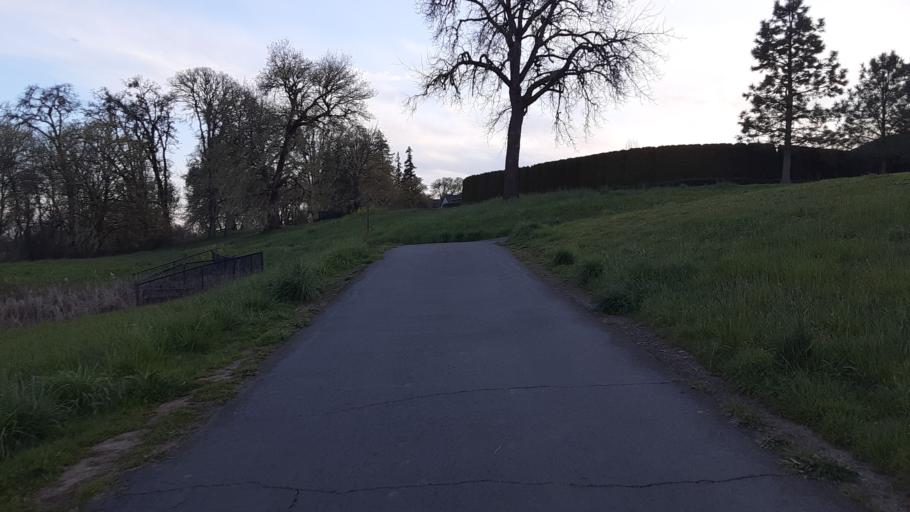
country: US
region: Oregon
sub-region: Benton County
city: Corvallis
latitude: 44.5298
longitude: -123.2546
